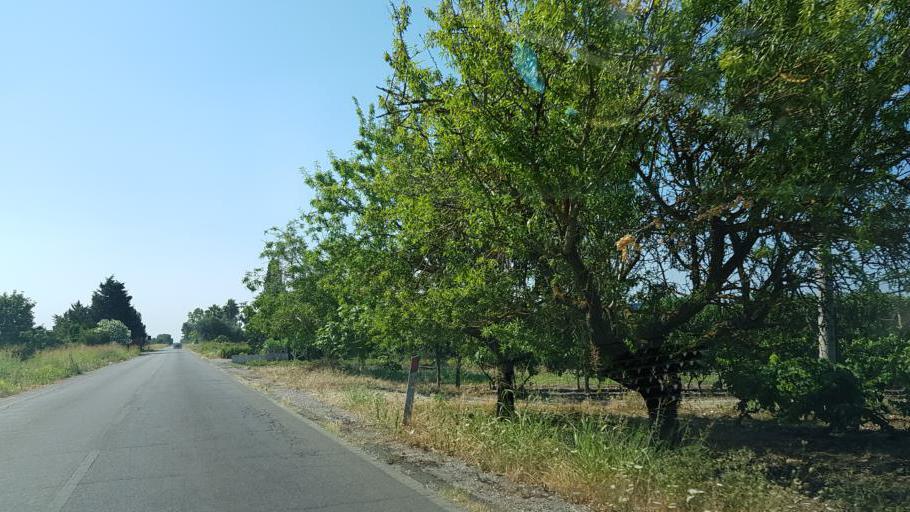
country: IT
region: Apulia
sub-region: Provincia di Brindisi
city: San Donaci
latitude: 40.4368
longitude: 17.9340
